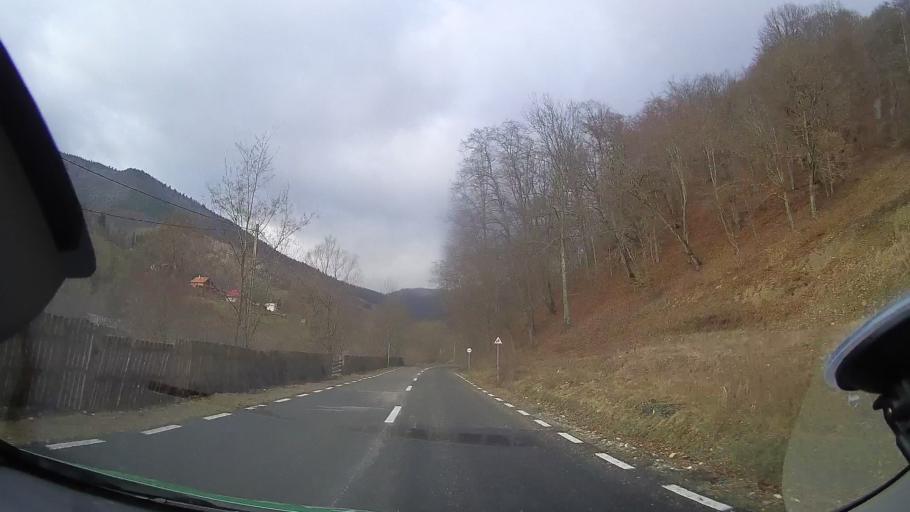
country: RO
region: Cluj
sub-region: Comuna Valea Ierii
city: Valea Ierii
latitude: 46.6397
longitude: 23.3605
